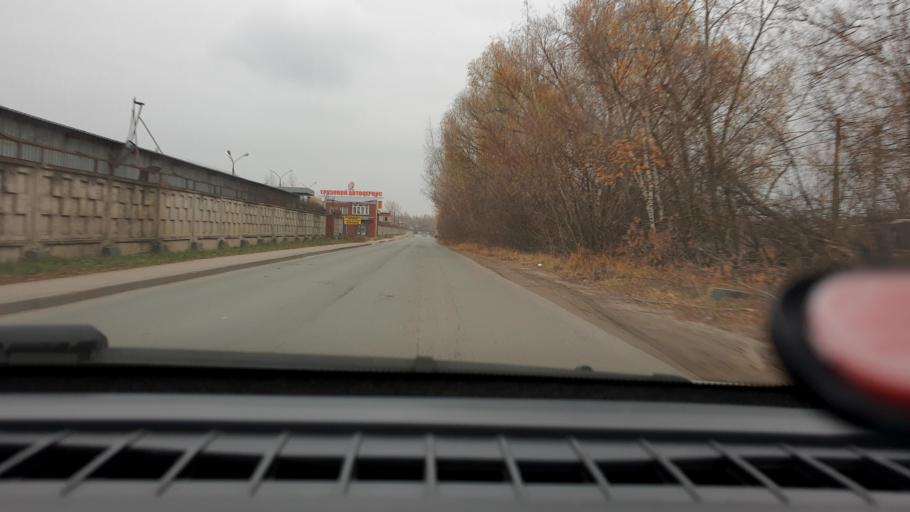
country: RU
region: Nizjnij Novgorod
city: Gorbatovka
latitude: 56.3364
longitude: 43.8063
